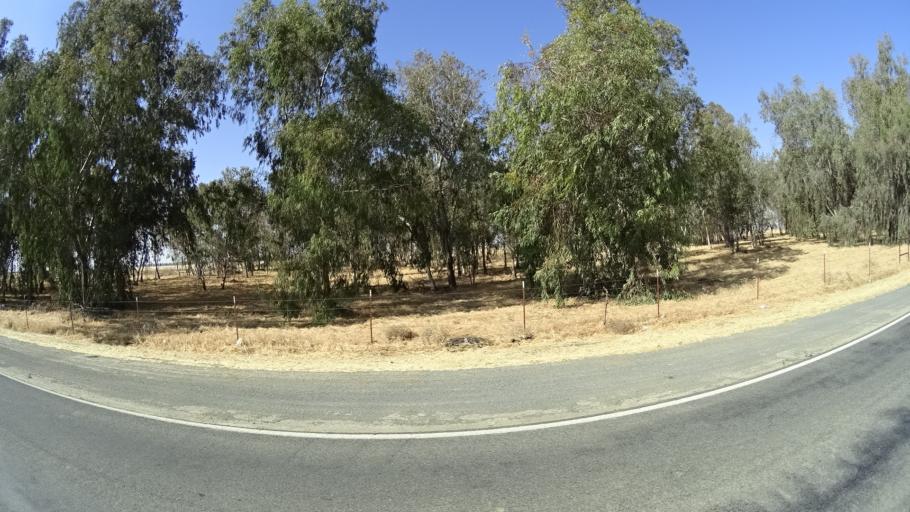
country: US
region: California
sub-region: Fresno County
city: Riverdale
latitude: 36.3613
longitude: -119.9129
